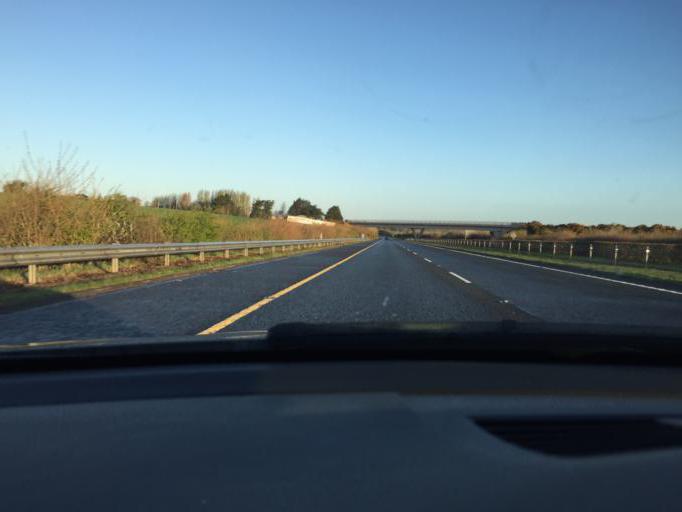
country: IE
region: Leinster
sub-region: An Mhi
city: Stamullin
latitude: 53.6516
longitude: -6.2850
